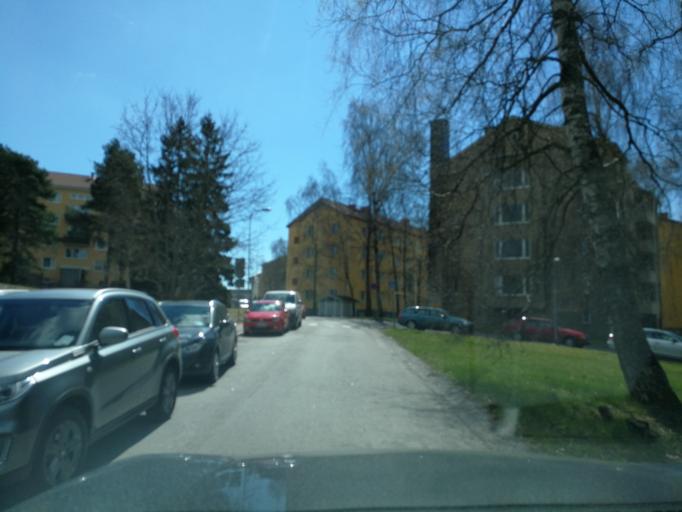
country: FI
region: Uusimaa
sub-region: Helsinki
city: Teekkarikylae
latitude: 60.1625
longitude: 24.8804
